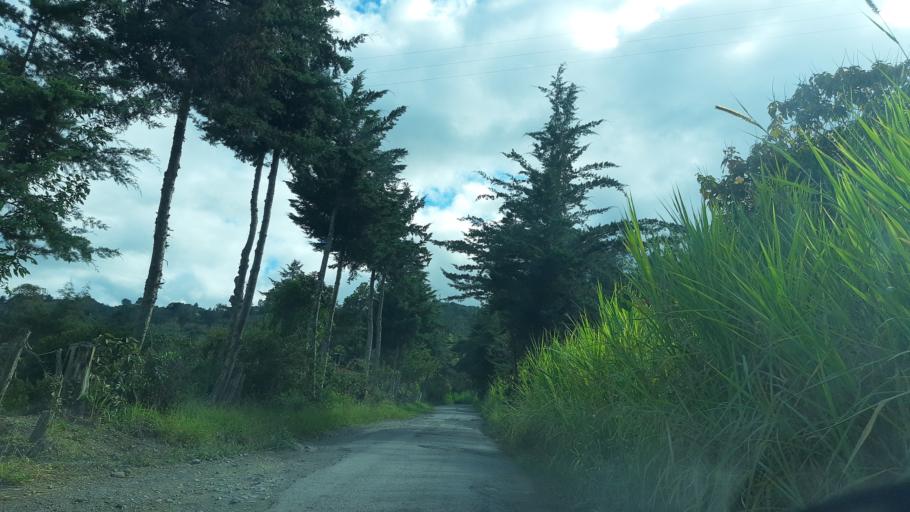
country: CO
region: Cundinamarca
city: Tenza
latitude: 5.0508
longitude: -73.4188
